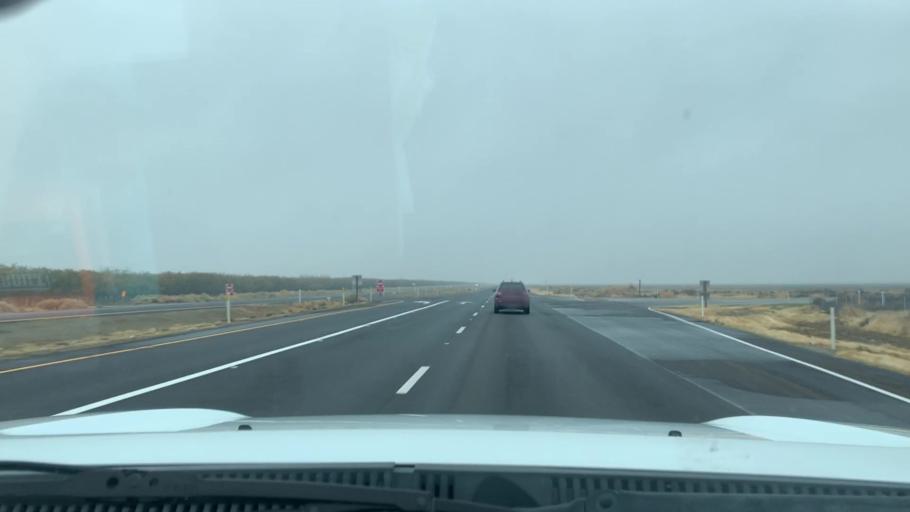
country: US
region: California
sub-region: Kern County
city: Lost Hills
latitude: 35.6145
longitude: -119.9237
